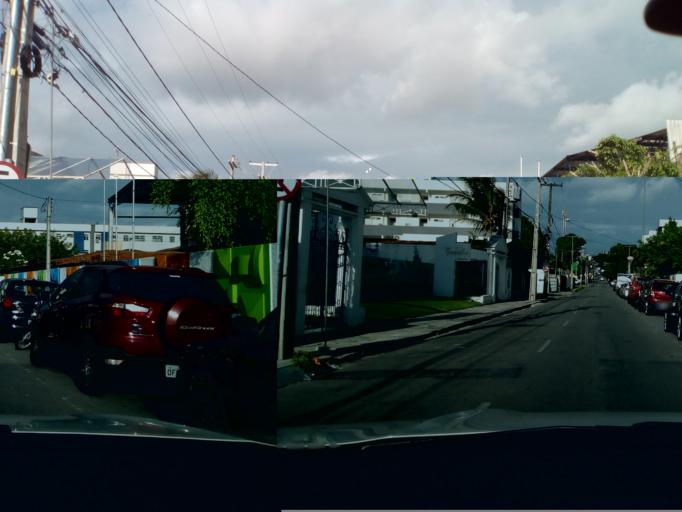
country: BR
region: Paraiba
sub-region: Joao Pessoa
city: Joao Pessoa
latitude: -7.1176
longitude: -34.8568
